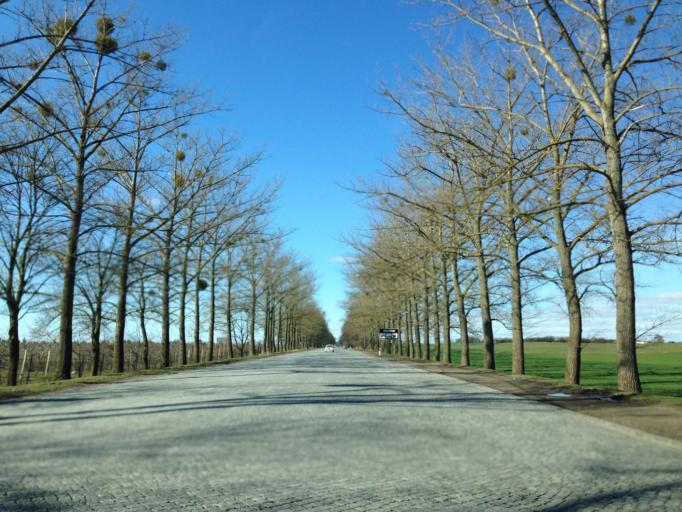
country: PL
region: Pomeranian Voivodeship
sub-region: Powiat tczewski
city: Tczew
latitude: 54.0506
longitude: 18.8011
